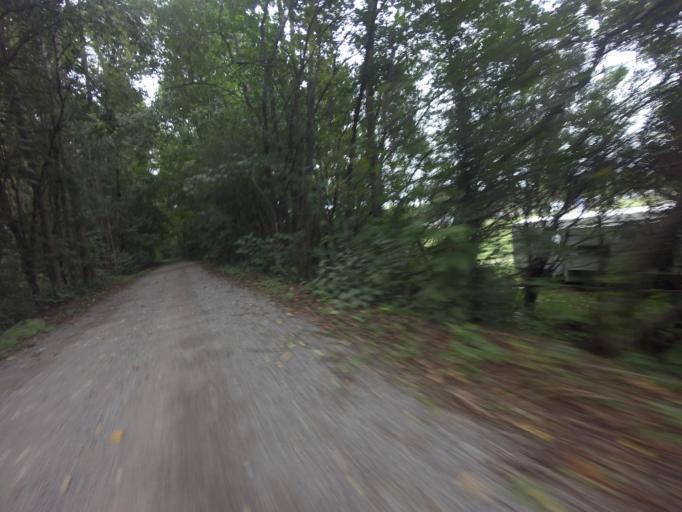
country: CA
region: Ontario
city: Omemee
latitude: 44.3964
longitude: -78.7567
